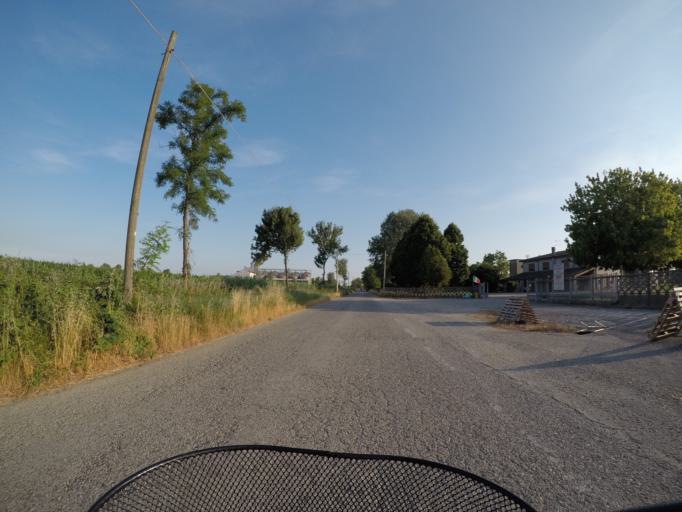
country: IT
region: Veneto
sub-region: Provincia di Rovigo
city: Fratta Polesine
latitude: 45.0278
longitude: 11.6239
